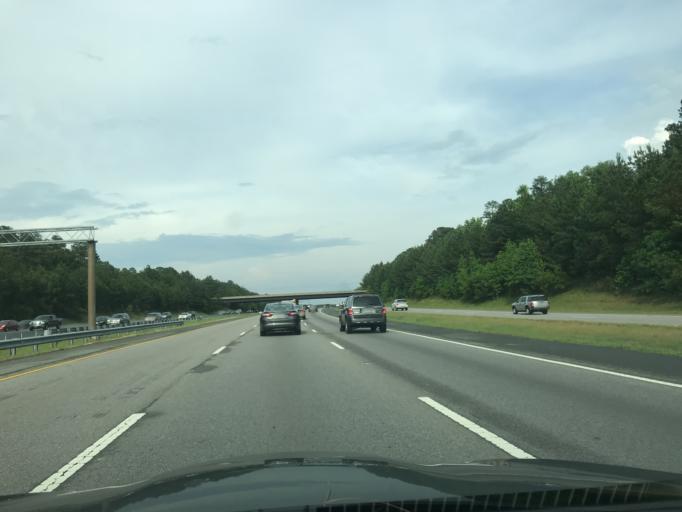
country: US
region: North Carolina
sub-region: Wake County
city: Morrisville
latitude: 35.8943
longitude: -78.8071
